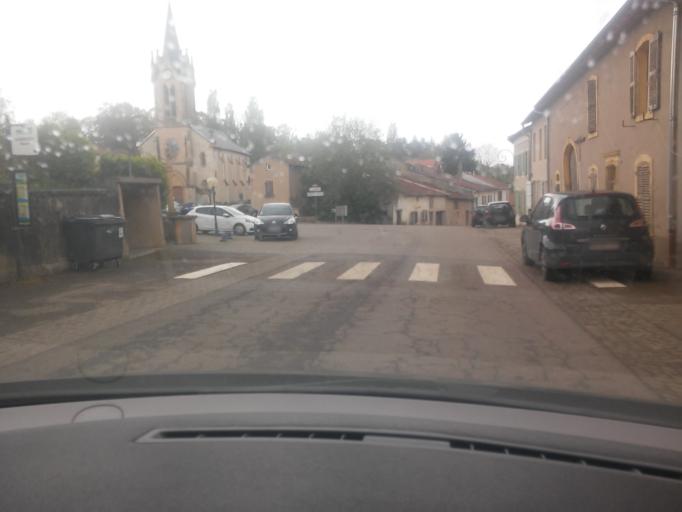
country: FR
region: Lorraine
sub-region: Departement de la Moselle
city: Verny
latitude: 49.0131
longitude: 6.2358
